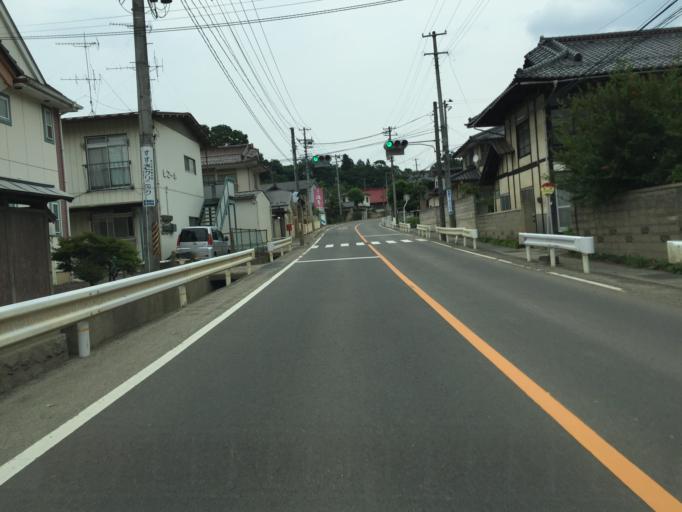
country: JP
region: Fukushima
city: Fukushima-shi
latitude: 37.6894
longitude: 140.4581
